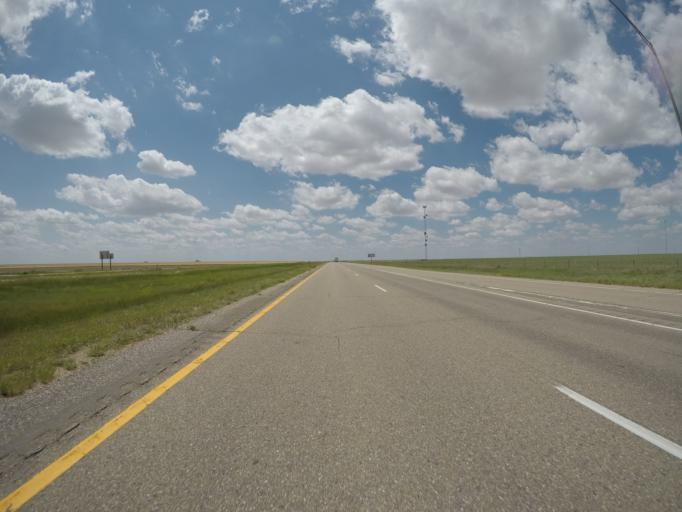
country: US
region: Colorado
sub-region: Kit Carson County
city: Burlington
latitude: 39.2941
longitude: -102.4322
